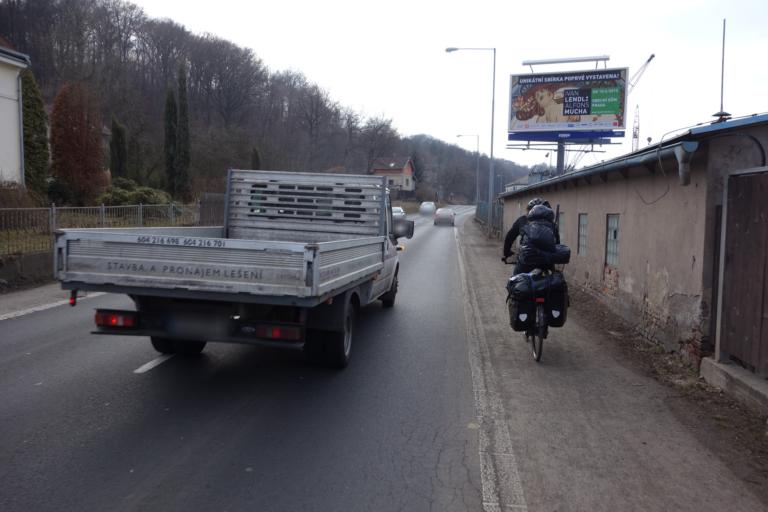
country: CZ
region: Ustecky
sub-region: Okres Usti nad Labem
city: Usti nad Labem
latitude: 50.6583
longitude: 14.0739
